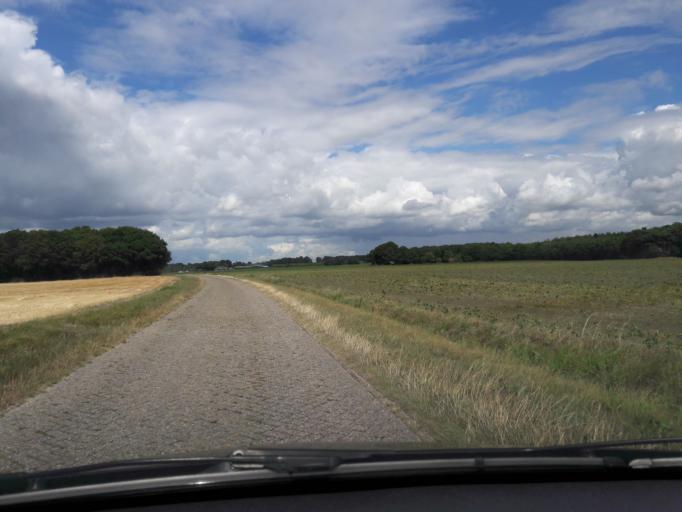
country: NL
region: Drenthe
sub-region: Gemeente Borger-Odoorn
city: Borger
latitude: 52.9400
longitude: 6.7971
